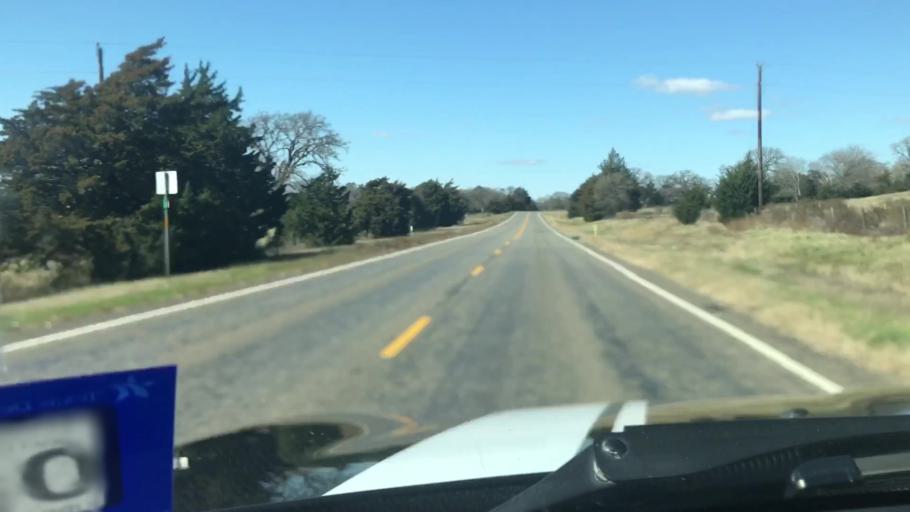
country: US
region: Texas
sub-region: Robertson County
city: Calvert
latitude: 30.8768
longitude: -96.7307
